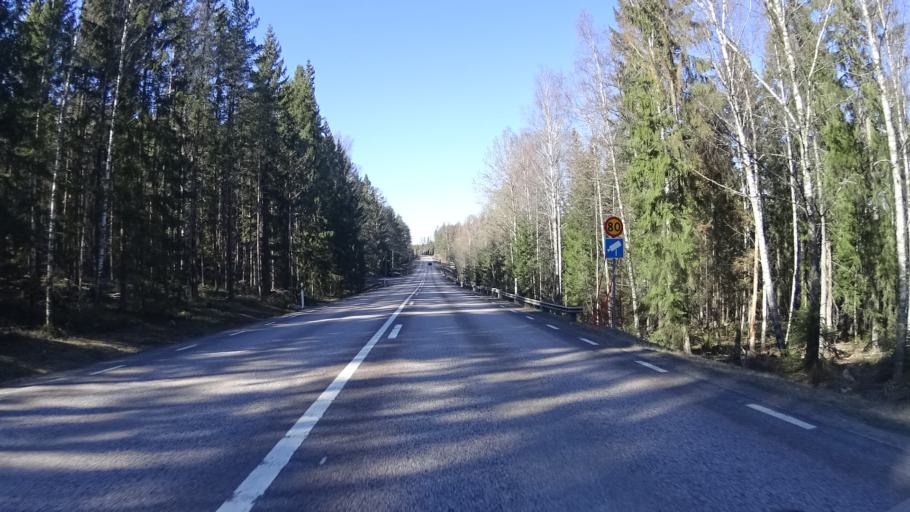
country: SE
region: Vaermland
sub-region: Karlstads Kommun
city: Edsvalla
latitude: 59.5900
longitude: 13.0108
